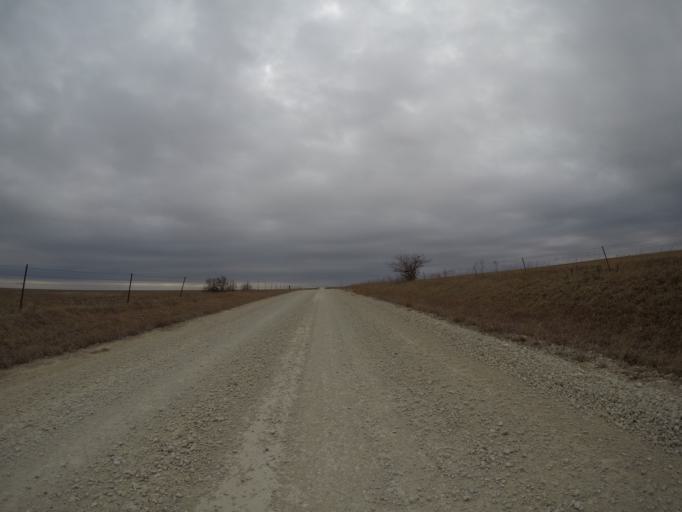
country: US
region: Kansas
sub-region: Wabaunsee County
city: Alma
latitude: 38.7641
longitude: -96.1496
